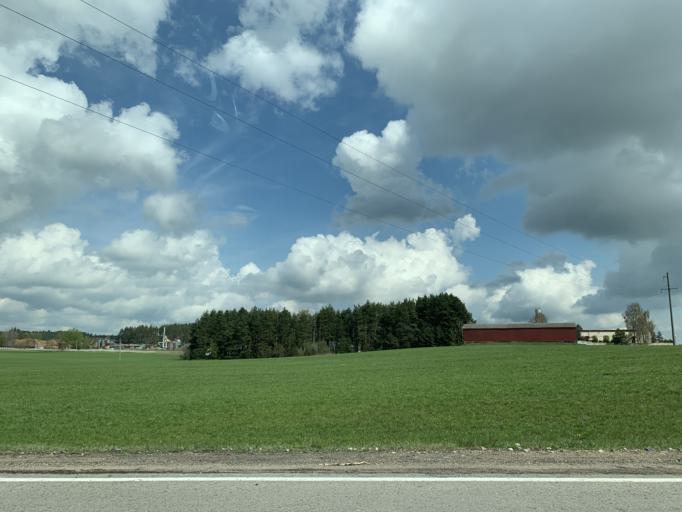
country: BY
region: Minsk
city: Nyasvizh
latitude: 53.2513
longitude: 26.6860
